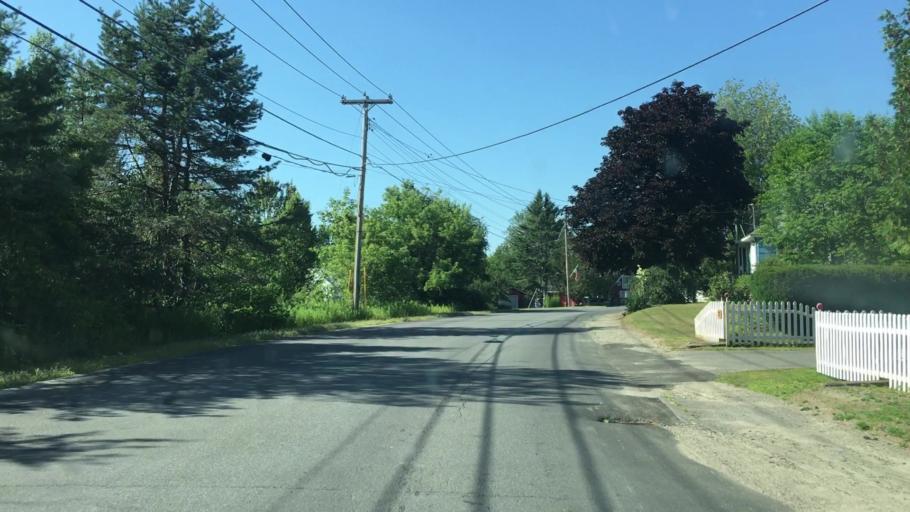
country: US
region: Maine
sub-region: Penobscot County
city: Howland
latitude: 45.2386
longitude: -68.6499
